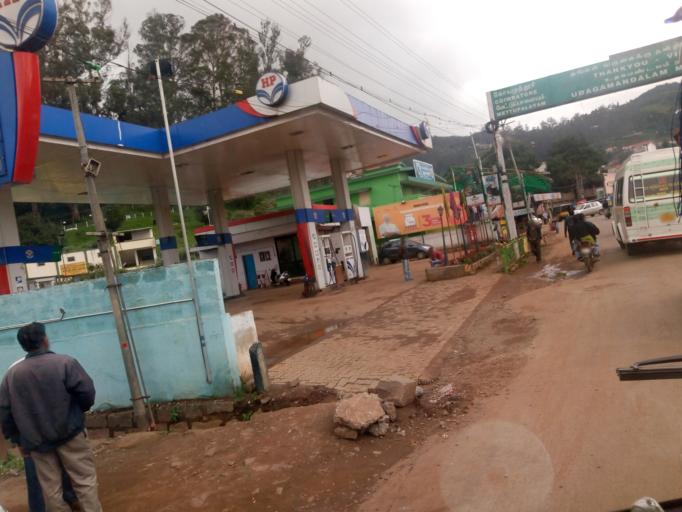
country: IN
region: Tamil Nadu
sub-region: Nilgiri
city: Ooty
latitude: 11.4115
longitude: 76.7095
